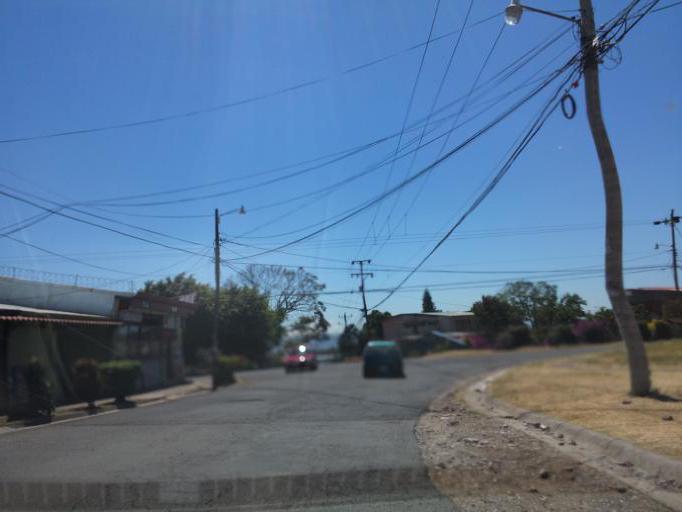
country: CR
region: Alajuela
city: Alajuela
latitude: 10.0100
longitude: -84.2250
